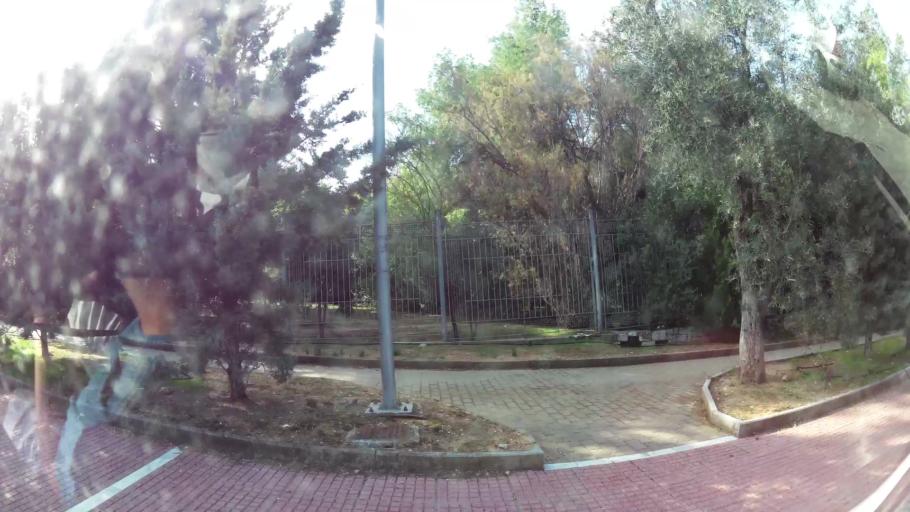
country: GR
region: Attica
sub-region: Nomarchia Athinas
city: Cholargos
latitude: 37.9950
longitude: 23.7934
